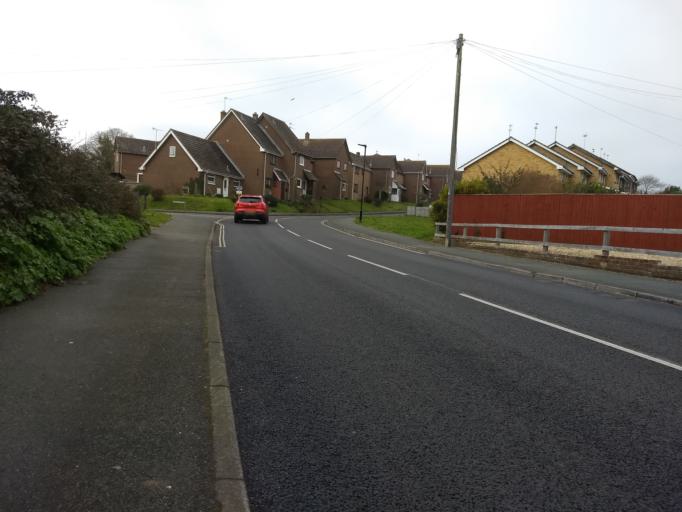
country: GB
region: England
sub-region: Isle of Wight
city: Sandown
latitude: 50.6628
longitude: -1.1542
